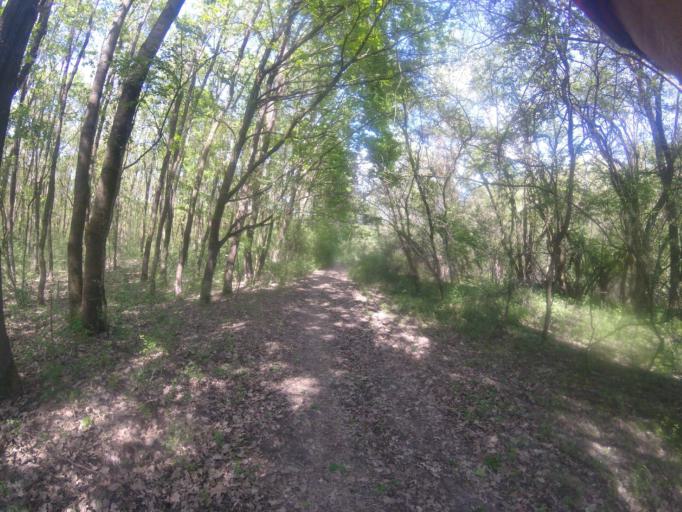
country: HU
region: Bekes
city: Gyula
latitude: 46.6456
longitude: 21.3057
